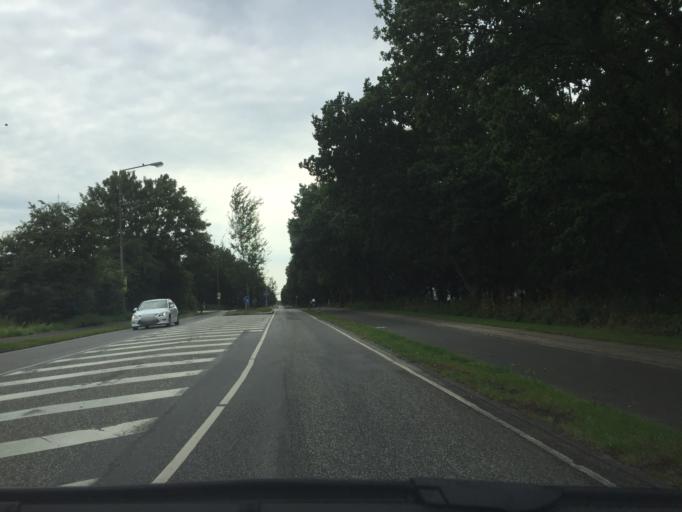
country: DK
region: Capital Region
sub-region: Lyngby-Tarbaek Kommune
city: Kongens Lyngby
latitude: 55.7886
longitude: 12.5278
